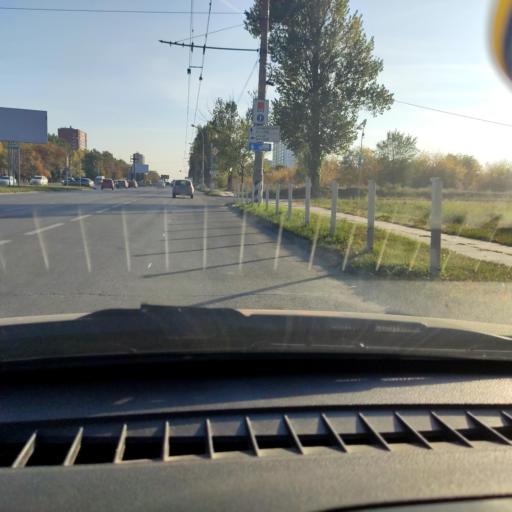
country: RU
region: Samara
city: Tol'yatti
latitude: 53.5178
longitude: 49.2581
